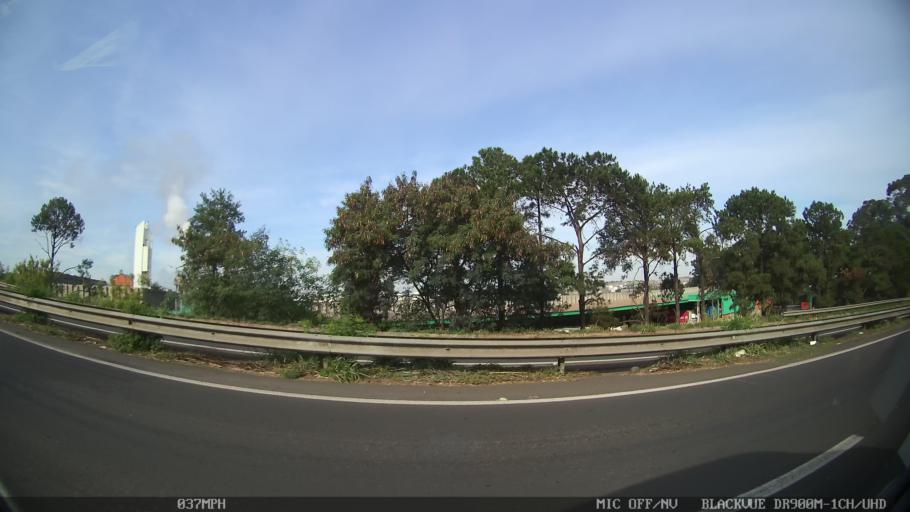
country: BR
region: Sao Paulo
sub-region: Piracicaba
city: Piracicaba
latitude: -22.6856
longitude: -47.6750
